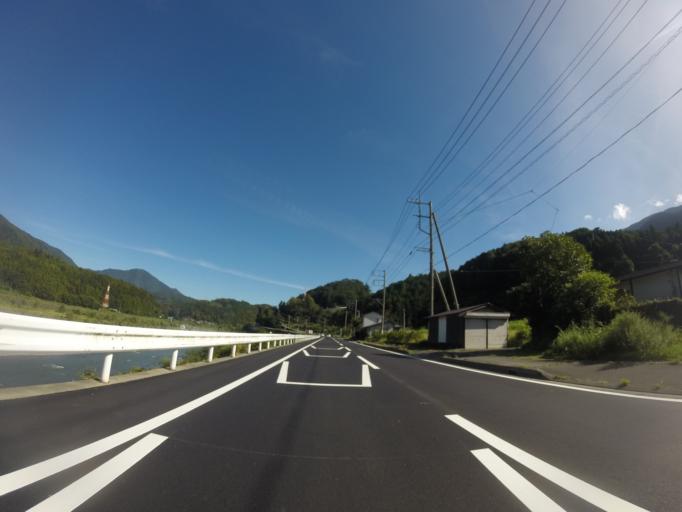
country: JP
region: Shizuoka
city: Fujinomiya
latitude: 35.3356
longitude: 138.4492
